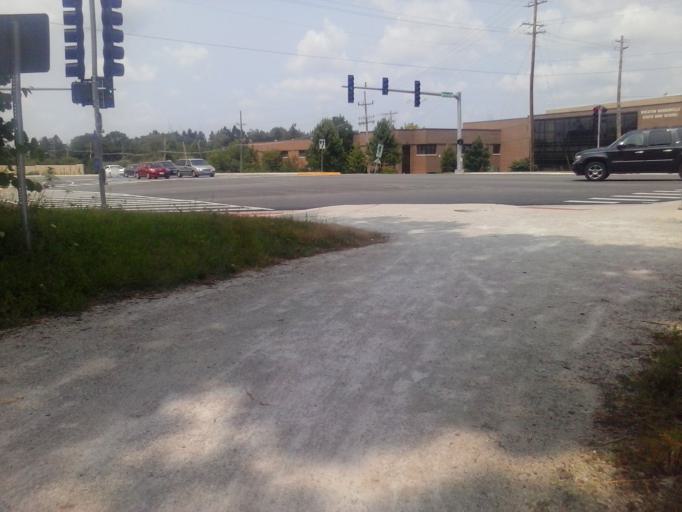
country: US
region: Illinois
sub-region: DuPage County
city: Warrenville
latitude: 41.8310
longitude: -88.1472
